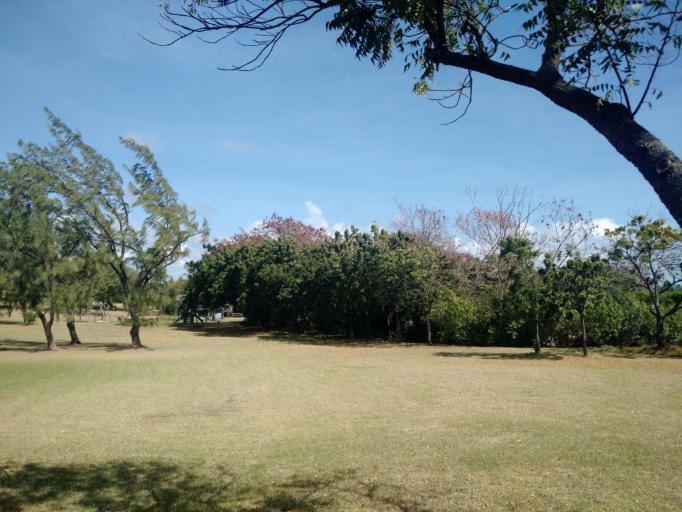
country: VC
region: Grenadines
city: Port Elizabeth
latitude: 12.8847
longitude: -61.1841
